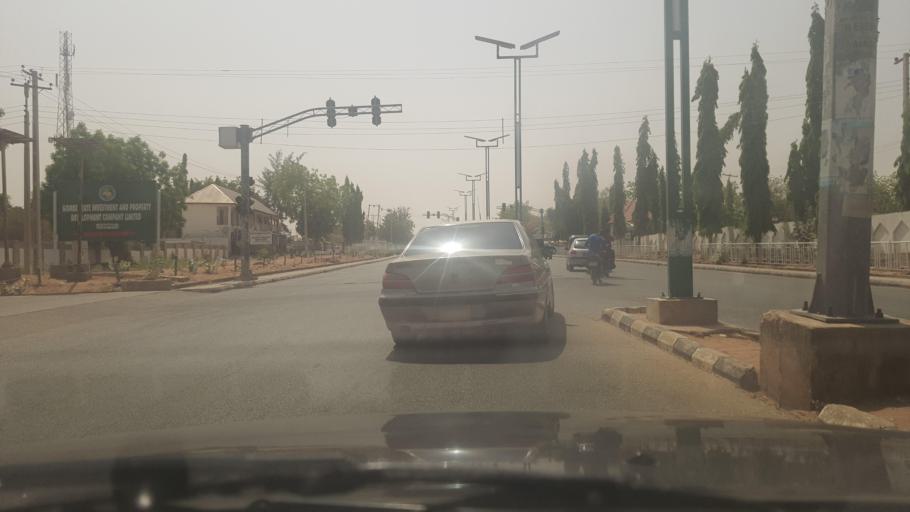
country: NG
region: Gombe
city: Gombe
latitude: 10.2847
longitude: 11.1477
